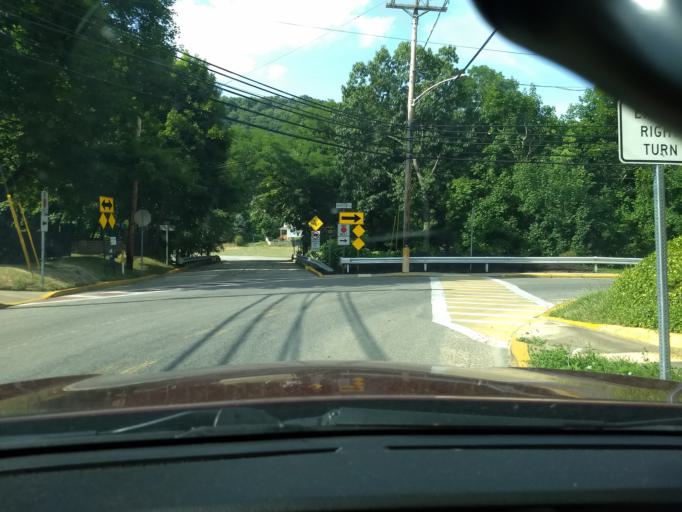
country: US
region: Pennsylvania
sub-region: Beaver County
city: Ambridge
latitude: 40.5808
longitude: -80.2165
